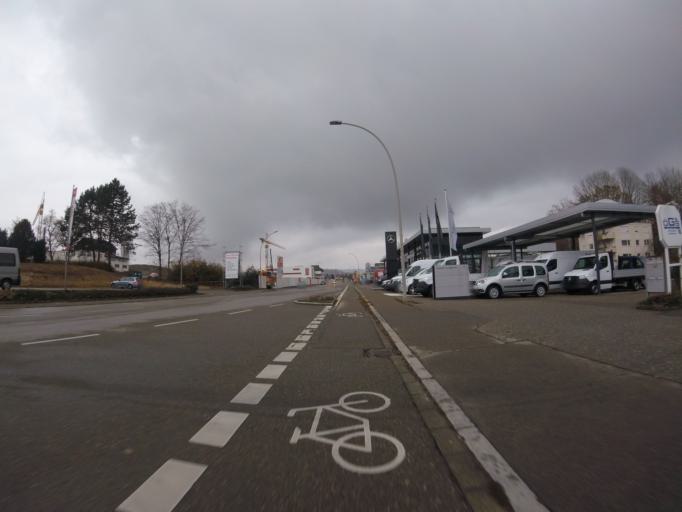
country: DE
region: Baden-Wuerttemberg
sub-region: Regierungsbezirk Stuttgart
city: Backnang
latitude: 48.9614
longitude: 9.4313
